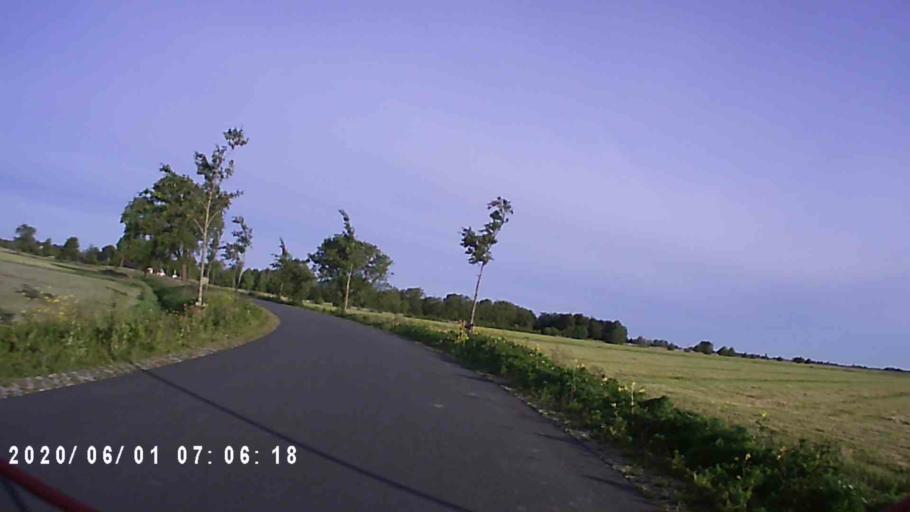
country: NL
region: Friesland
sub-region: Gemeente Kollumerland en Nieuwkruisland
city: Kollumerzwaag
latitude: 53.2993
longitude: 6.0819
